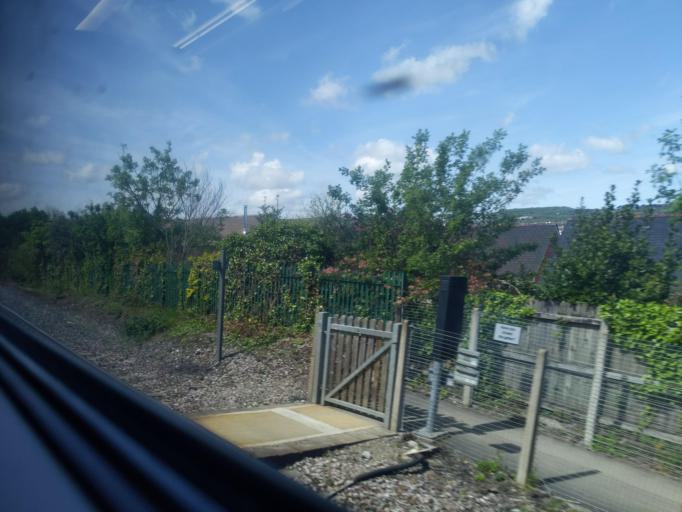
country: GB
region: England
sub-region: Cornwall
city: St Austell
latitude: 50.3378
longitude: -4.7624
